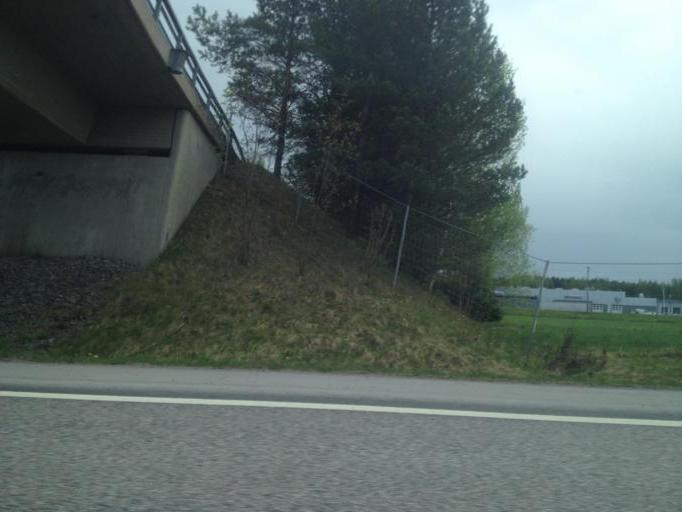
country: FI
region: Uusimaa
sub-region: Helsinki
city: Hyvinge
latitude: 60.6113
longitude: 24.8053
